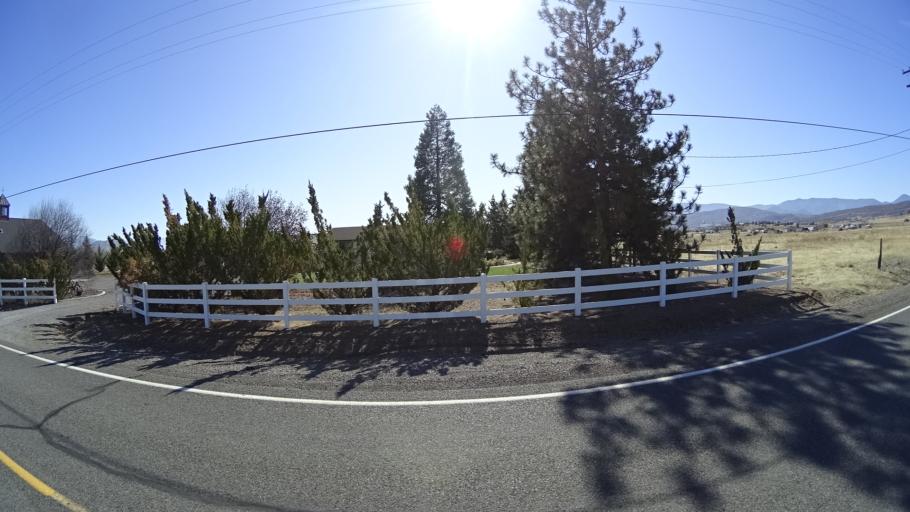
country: US
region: California
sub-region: Siskiyou County
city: Yreka
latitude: 41.7430
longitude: -122.5909
